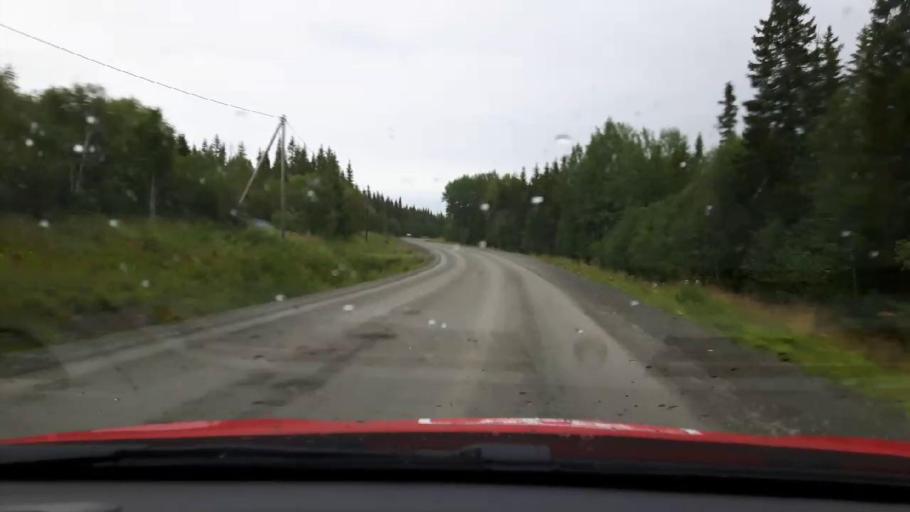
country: SE
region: Jaemtland
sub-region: Are Kommun
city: Are
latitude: 63.4547
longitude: 12.6462
